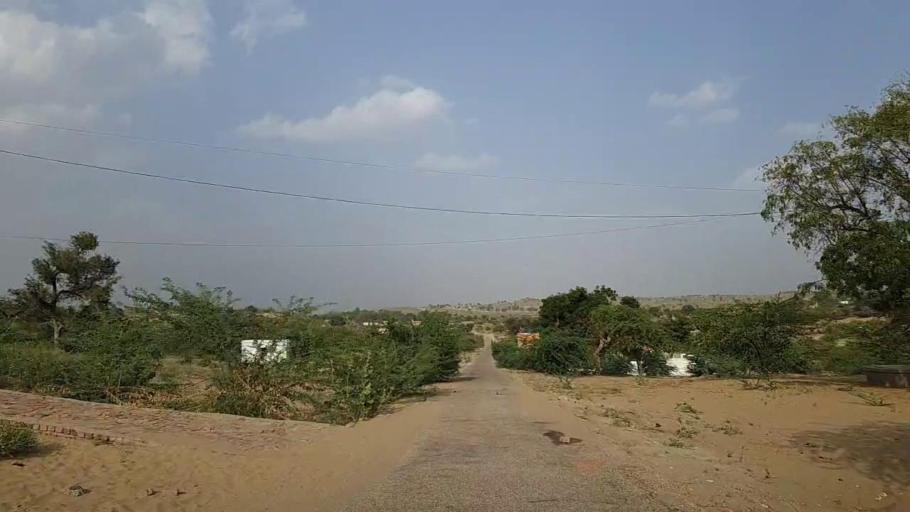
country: PK
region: Sindh
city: Islamkot
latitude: 24.7747
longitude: 70.1870
